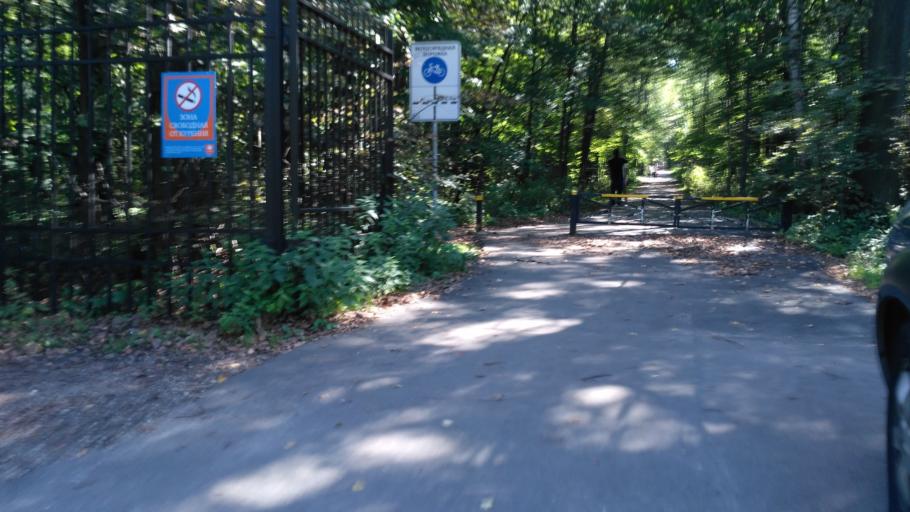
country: RU
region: Moscow
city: Metrogorodok
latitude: 55.7768
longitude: 37.7590
